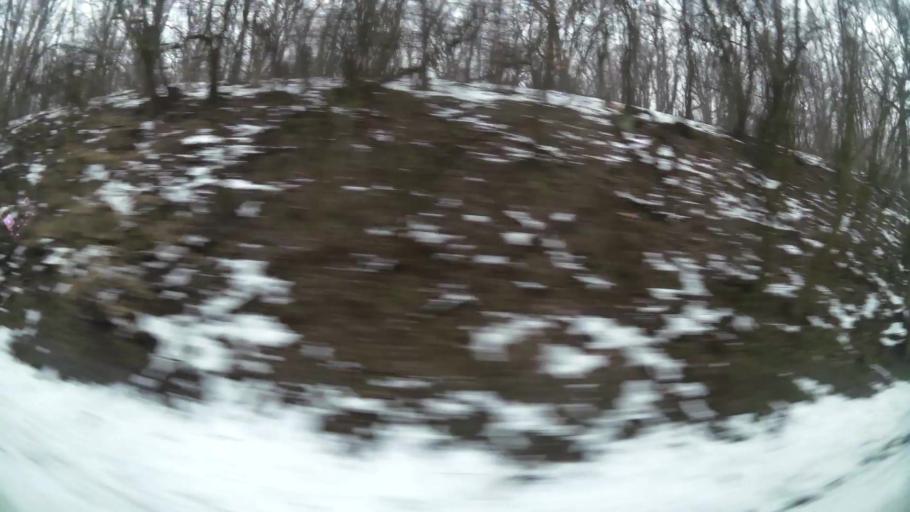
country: RS
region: Central Serbia
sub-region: Belgrade
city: Cukarica
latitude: 44.7712
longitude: 20.4357
